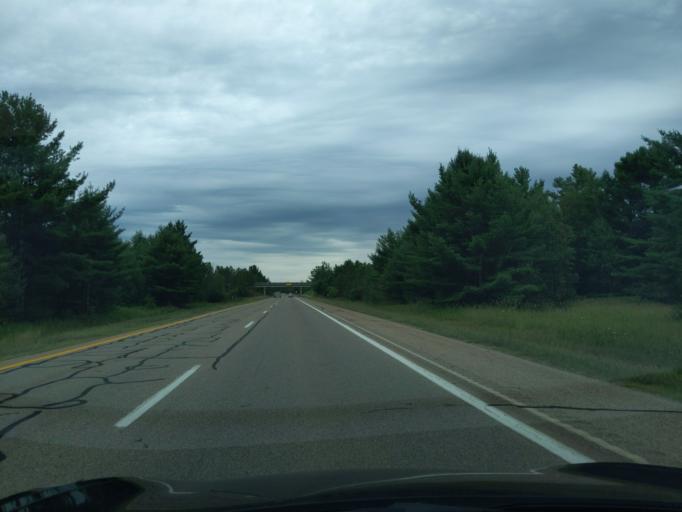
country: US
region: Michigan
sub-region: Roscommon County
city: Houghton Lake
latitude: 44.2722
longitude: -84.8018
